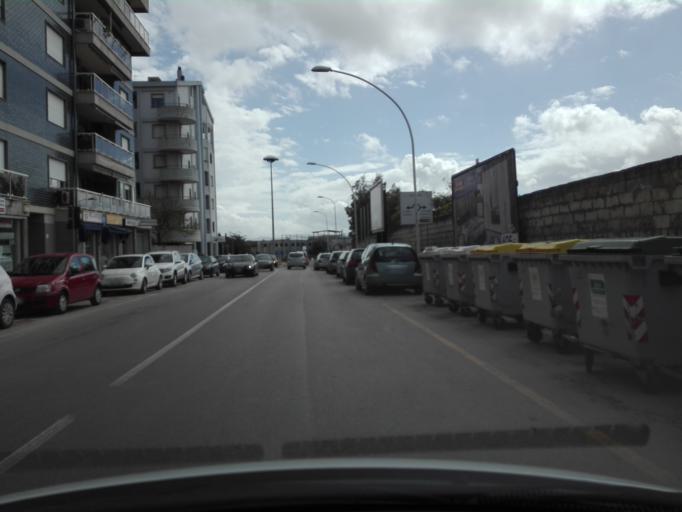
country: IT
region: Sardinia
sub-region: Provincia di Sassari
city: Sassari
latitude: 40.7253
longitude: 8.5761
